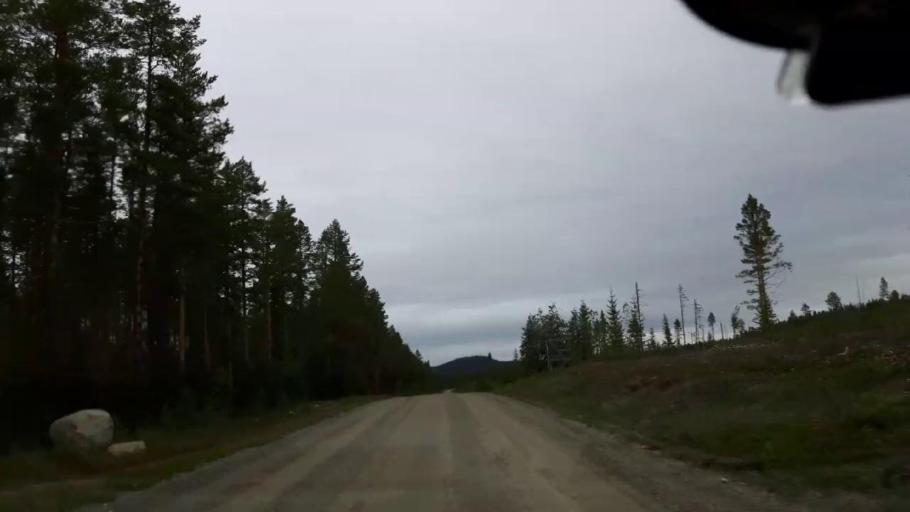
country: SE
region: Vaesternorrland
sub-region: Ange Kommun
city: Fransta
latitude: 62.8606
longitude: 16.0423
